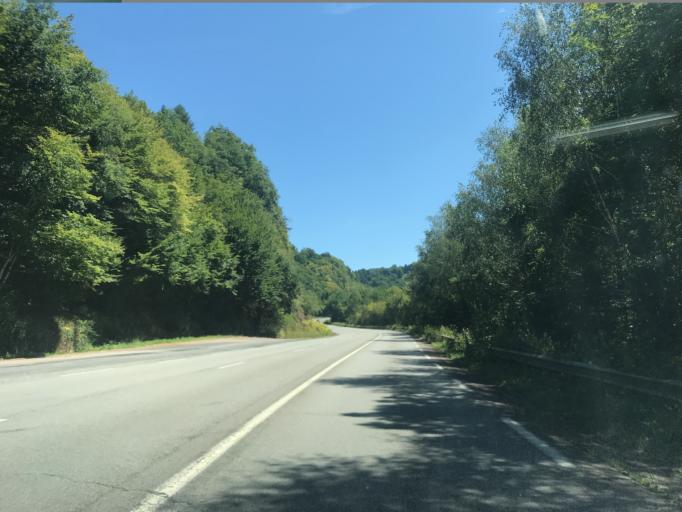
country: FR
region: Limousin
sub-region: Departement de la Correze
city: Chameyrat
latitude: 45.2326
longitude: 1.7182
